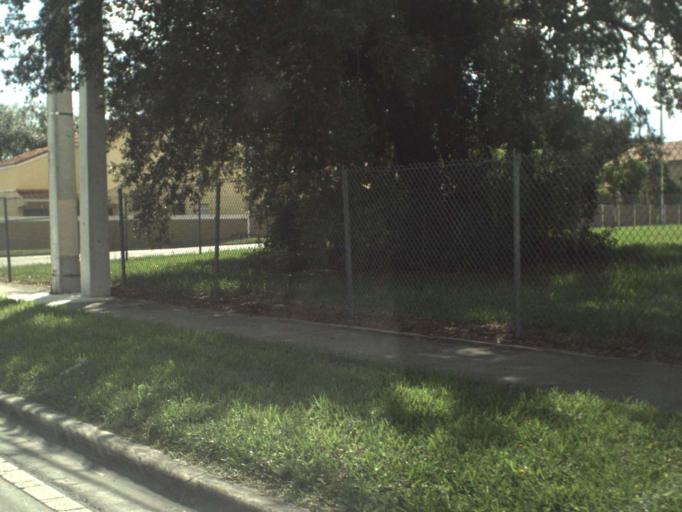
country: US
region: Florida
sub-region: Miami-Dade County
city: Sunset
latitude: 25.7008
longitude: -80.3726
